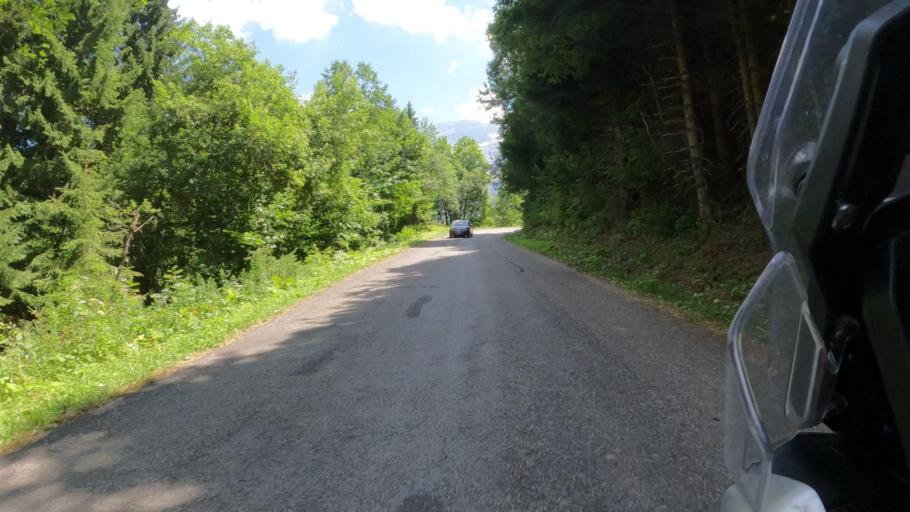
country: CH
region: Vaud
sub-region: Aigle District
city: Villars-sur-Ollon
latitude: 46.3461
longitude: 7.1456
